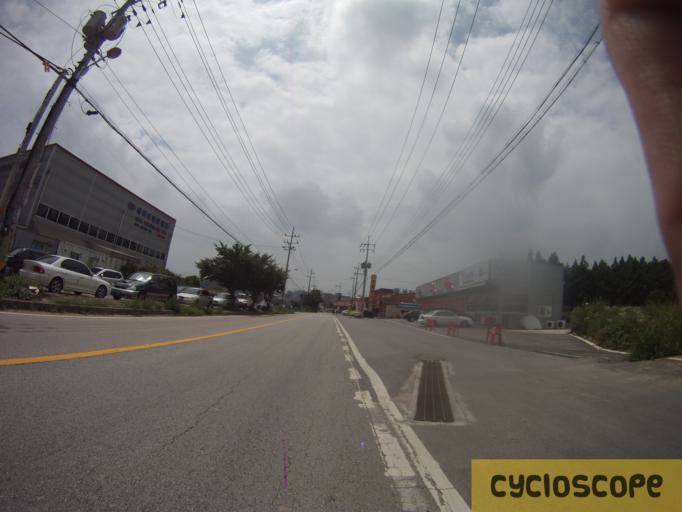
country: KR
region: Gyeonggi-do
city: Hwaseong-si
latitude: 37.1683
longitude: 126.9298
